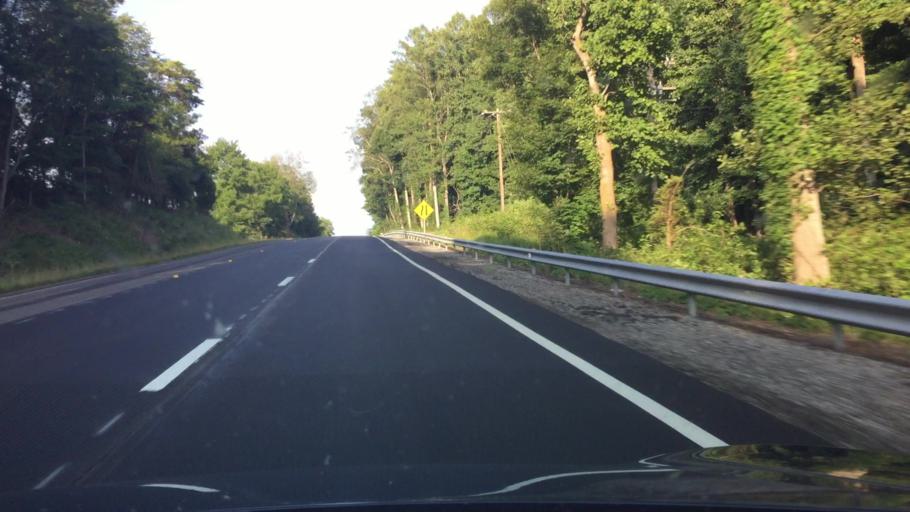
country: US
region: Virginia
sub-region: Montgomery County
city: Christiansburg
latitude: 37.1313
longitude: -80.4750
